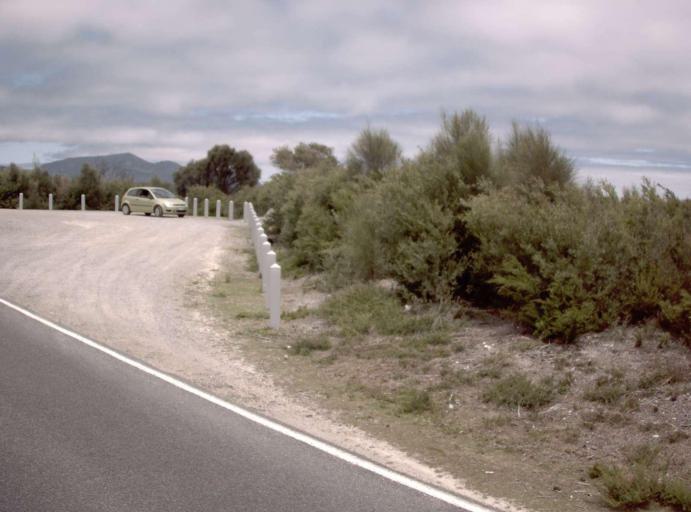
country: AU
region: Victoria
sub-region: Latrobe
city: Morwell
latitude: -39.0150
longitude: 146.2988
